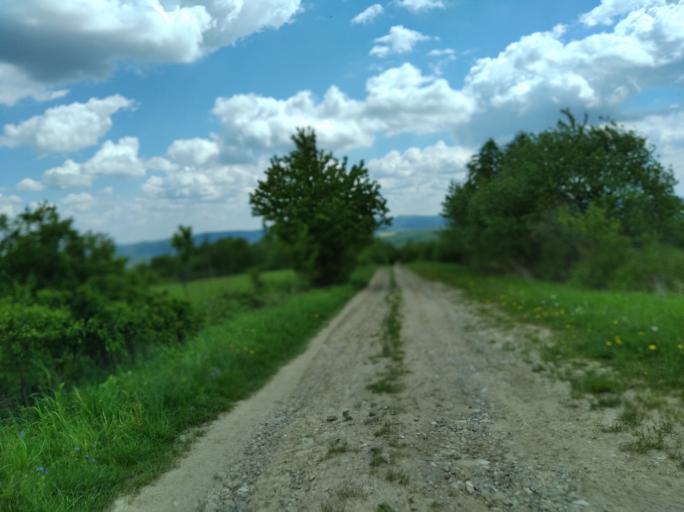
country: PL
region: Subcarpathian Voivodeship
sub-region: Powiat strzyzowski
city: Frysztak
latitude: 49.8334
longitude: 21.5413
